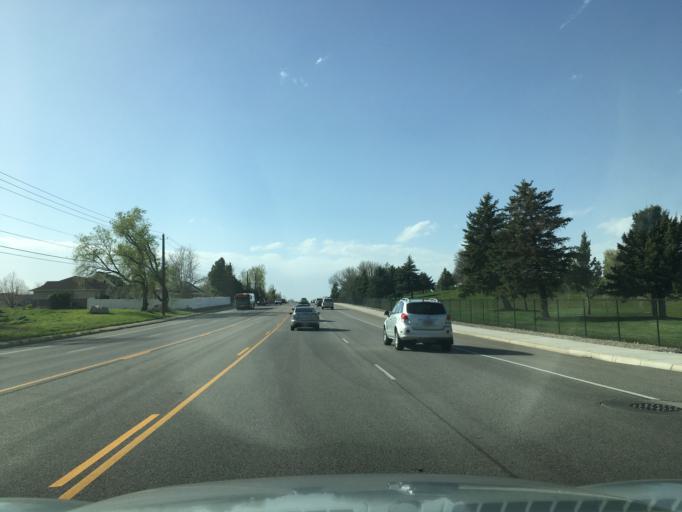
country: US
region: Utah
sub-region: Davis County
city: Fruit Heights
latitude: 41.0172
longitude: -111.9194
